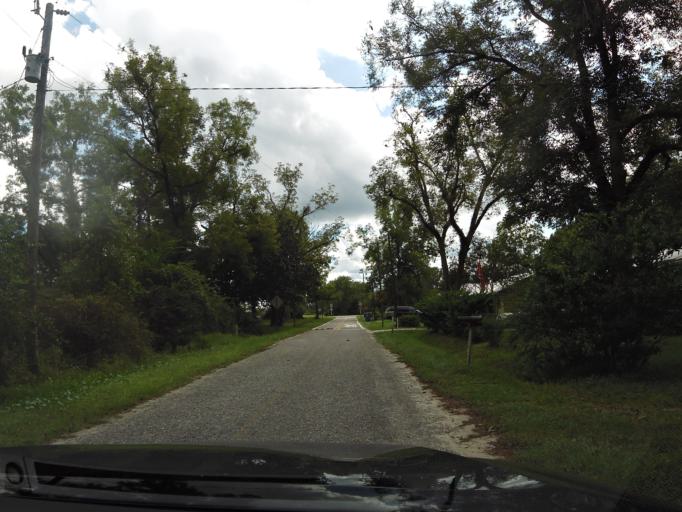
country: US
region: Georgia
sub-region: Brantley County
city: Nahunta
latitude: 31.2034
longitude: -81.9963
